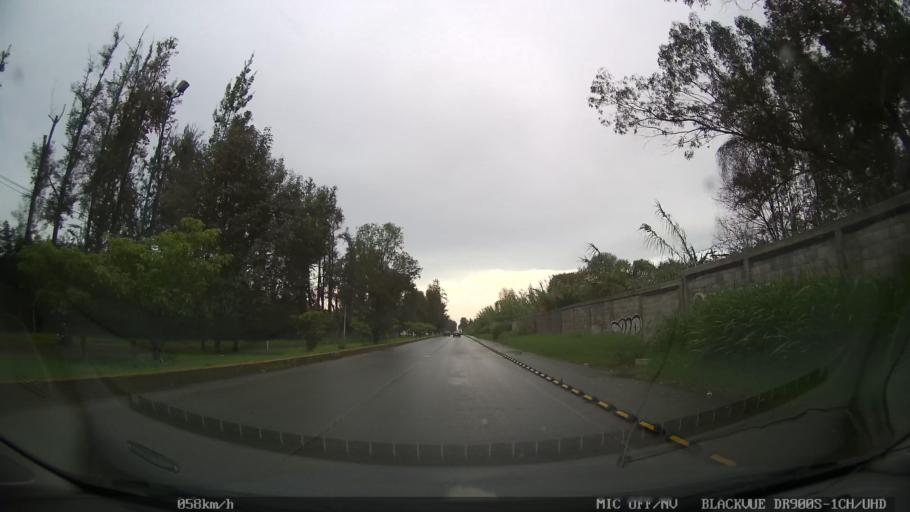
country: MX
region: Michoacan
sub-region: Uruapan
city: Santa Rosa (Santa Barbara)
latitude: 19.4023
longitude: -102.0324
